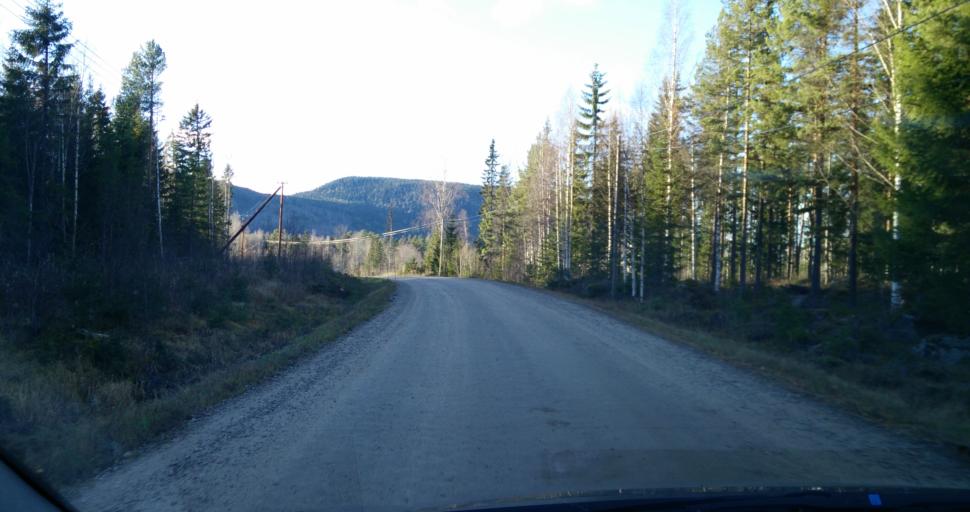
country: SE
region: Gaevleborg
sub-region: Nordanstigs Kommun
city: Bergsjoe
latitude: 62.0585
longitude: 16.8054
